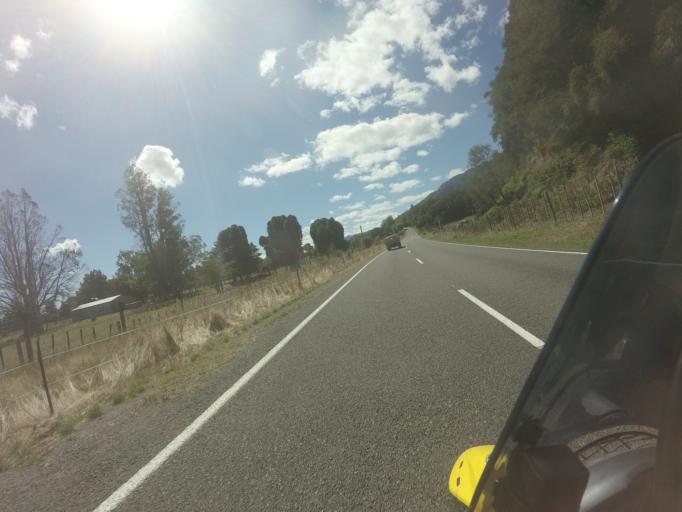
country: NZ
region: Bay of Plenty
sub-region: Whakatane District
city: Murupara
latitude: -38.4764
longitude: 176.7494
